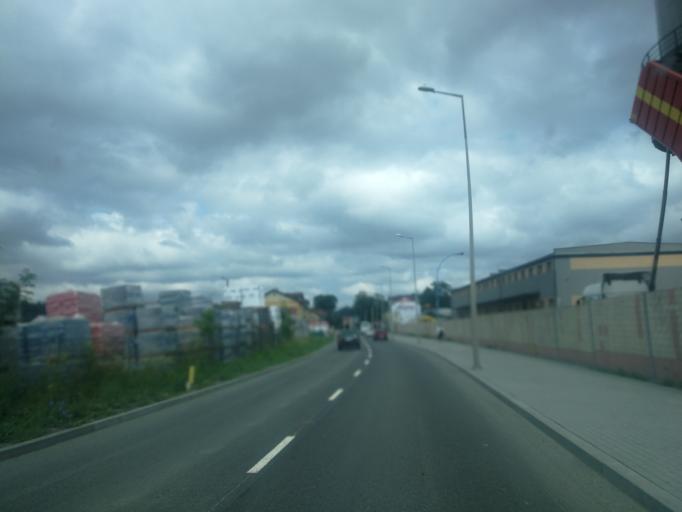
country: PL
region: Subcarpathian Voivodeship
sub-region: Powiat sanocki
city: Sanok
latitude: 49.5517
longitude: 22.2143
